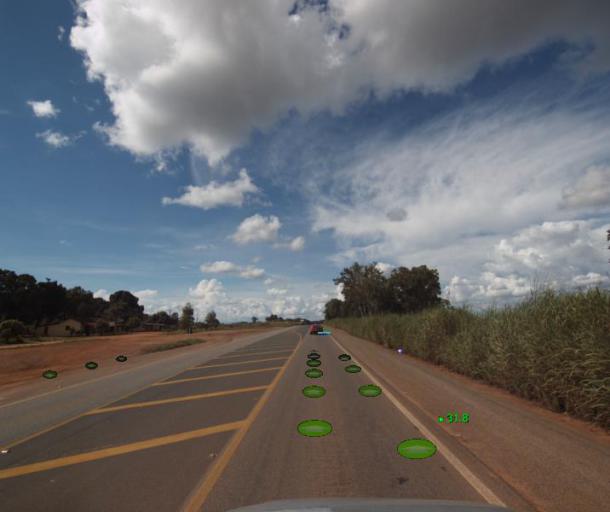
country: BR
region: Goias
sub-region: Porangatu
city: Porangatu
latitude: -13.1043
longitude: -49.1995
